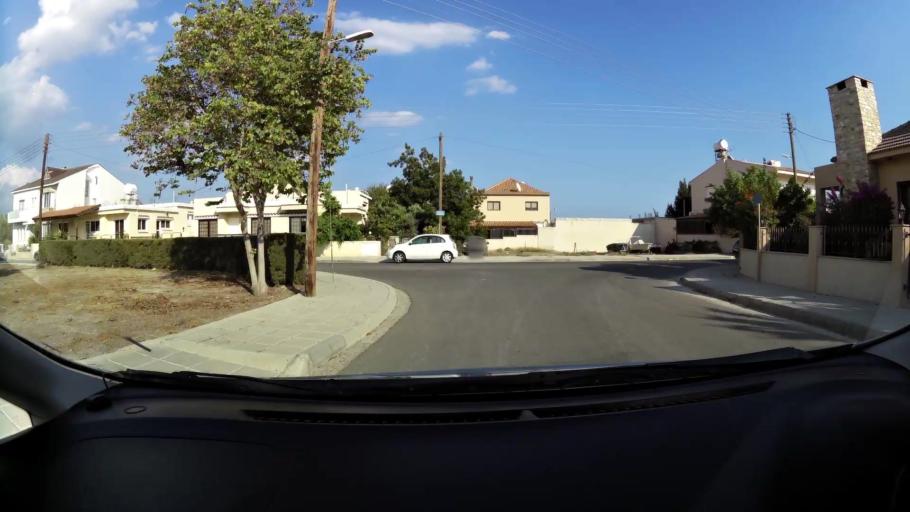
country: CY
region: Larnaka
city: Dhromolaxia
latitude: 34.8744
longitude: 33.5948
